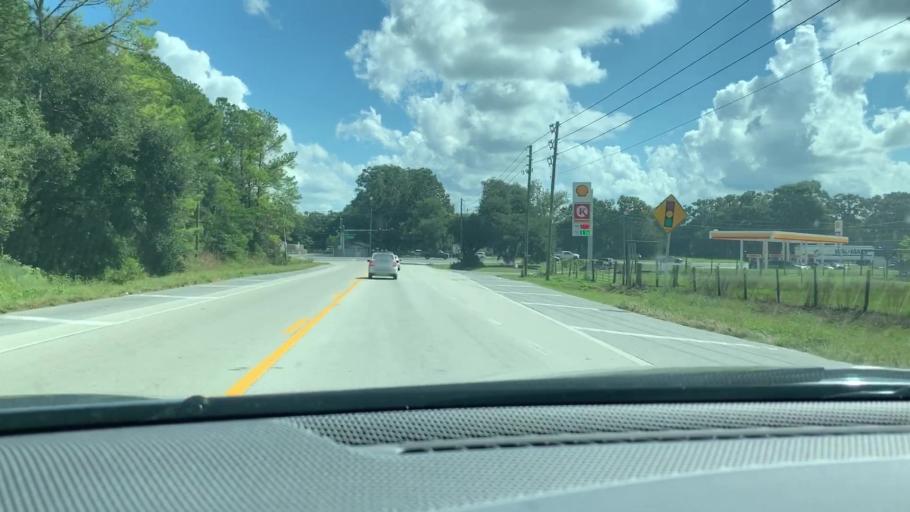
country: US
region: Florida
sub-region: Marion County
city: Ocala
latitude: 29.2668
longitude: -82.1537
